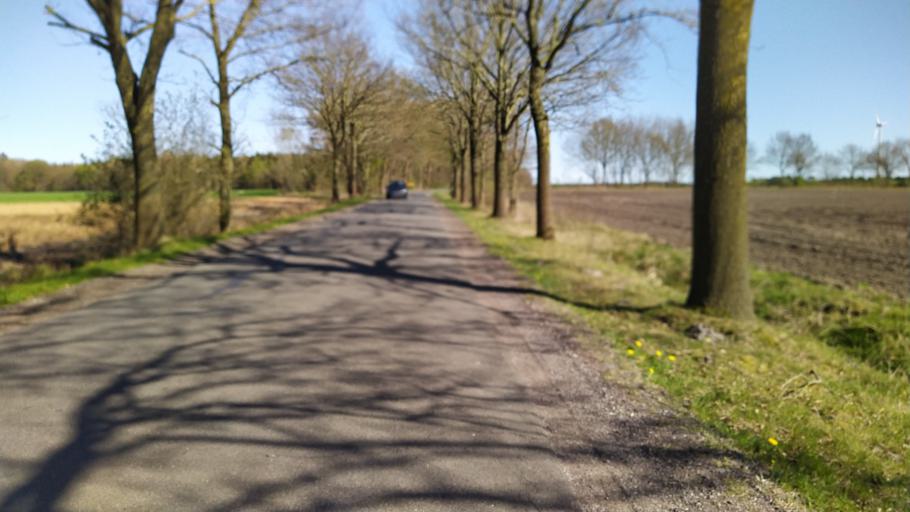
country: DE
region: Lower Saxony
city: Heeslingen
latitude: 53.3282
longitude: 9.3886
